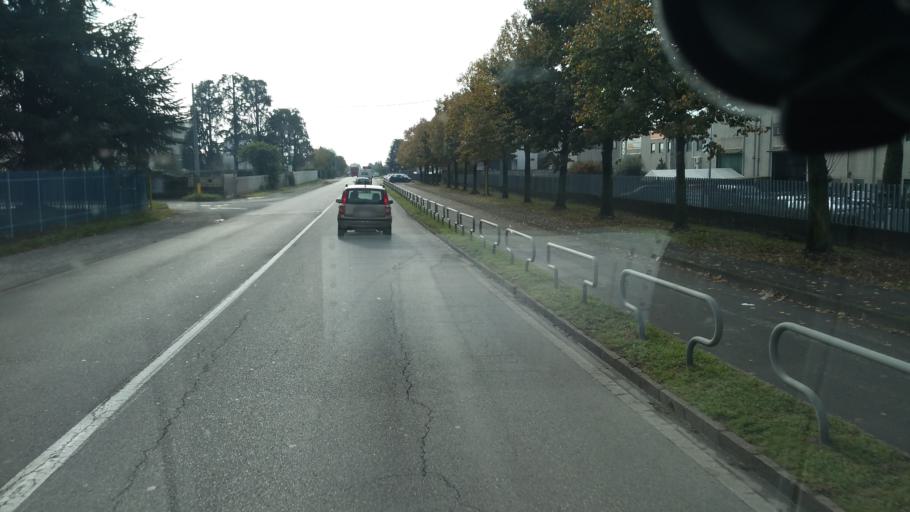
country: IT
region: Lombardy
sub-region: Provincia di Bergamo
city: Urgnano
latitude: 45.6130
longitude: 9.6940
